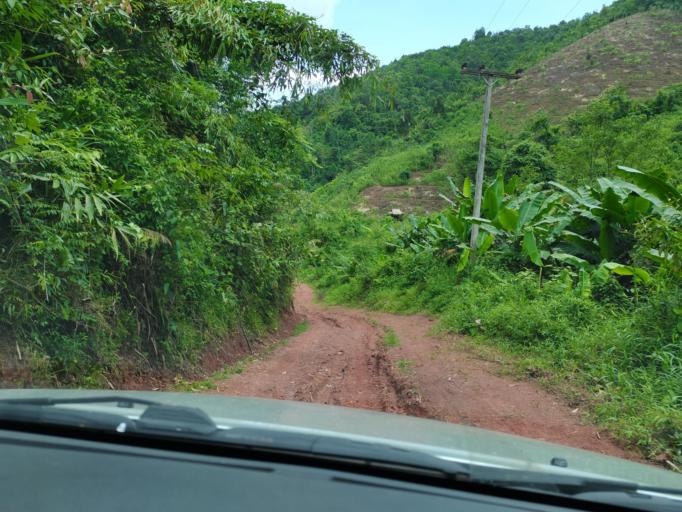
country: LA
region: Loungnamtha
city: Muang Nale
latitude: 20.5137
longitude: 101.0783
